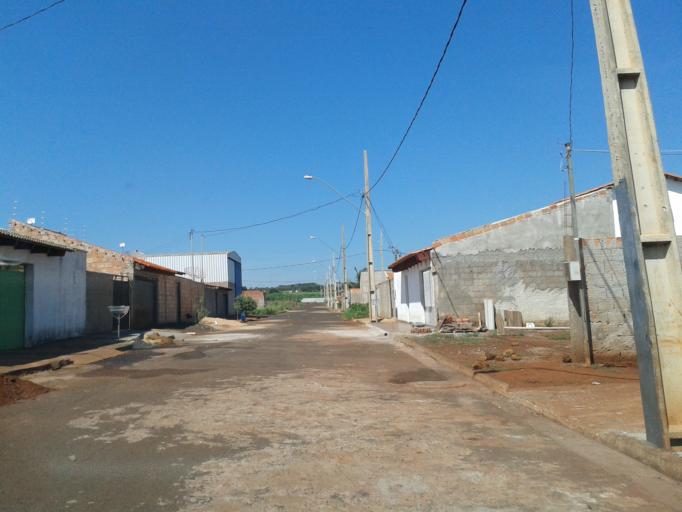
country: BR
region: Minas Gerais
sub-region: Centralina
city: Centralina
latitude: -18.5985
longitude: -49.1948
